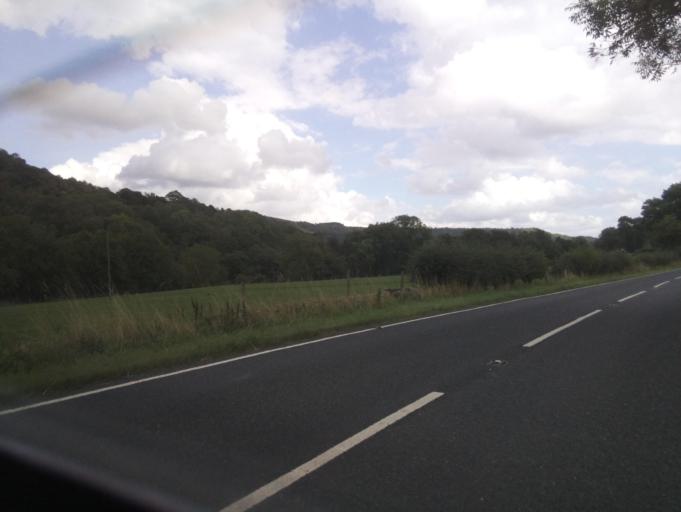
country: GB
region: England
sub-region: North Yorkshire
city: Leyburn
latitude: 54.4048
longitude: -1.8177
